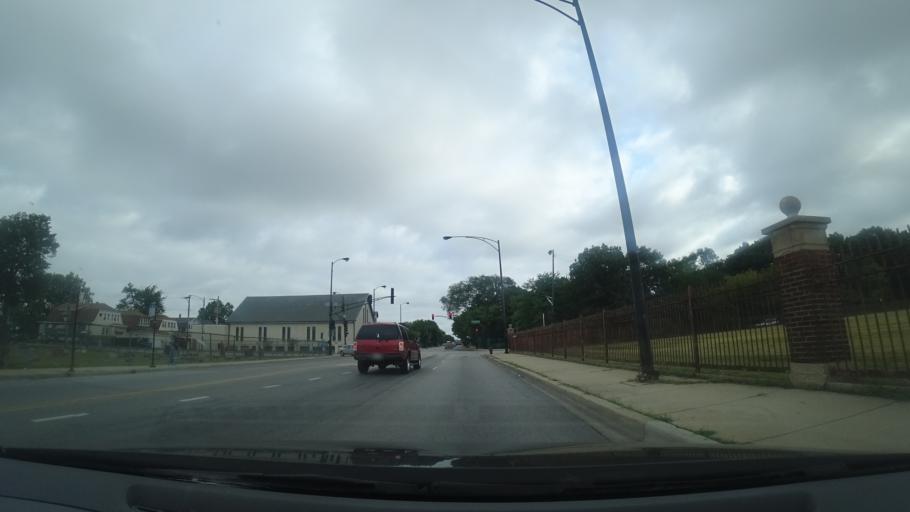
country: US
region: Illinois
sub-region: Cook County
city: Lincolnwood
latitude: 41.9824
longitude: -87.7284
